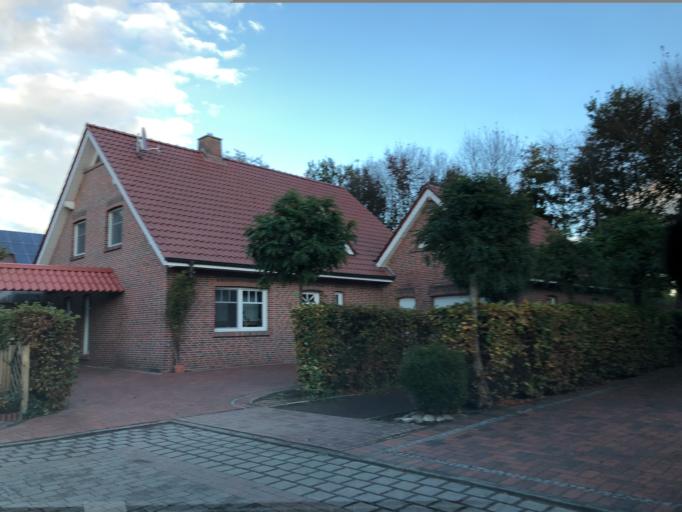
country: DE
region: Lower Saxony
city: Papenburg
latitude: 53.0834
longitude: 7.4178
